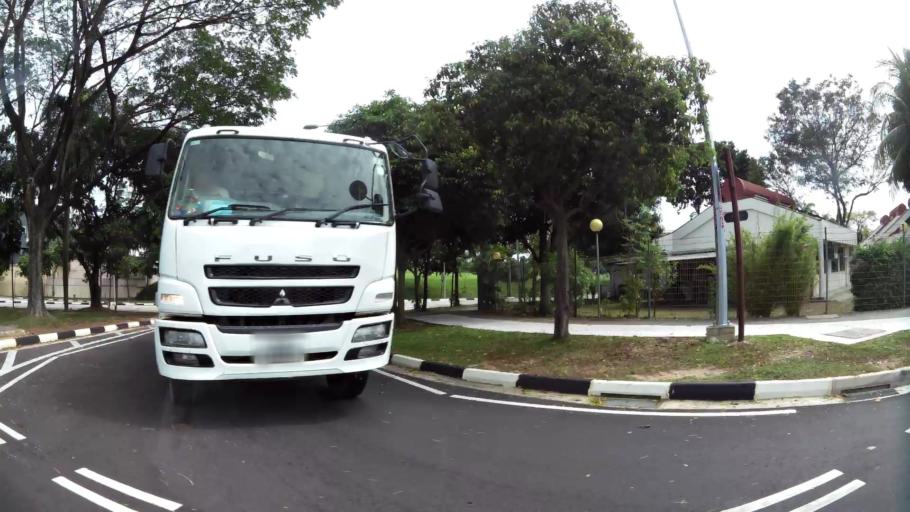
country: SG
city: Singapore
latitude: 1.3144
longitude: 103.7534
